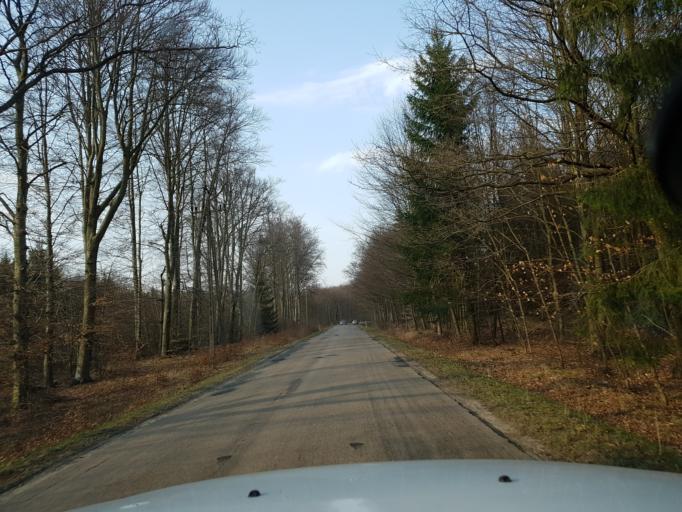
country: PL
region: West Pomeranian Voivodeship
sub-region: Powiat swidwinski
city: Polczyn-Zdroj
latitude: 53.7337
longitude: 16.0756
